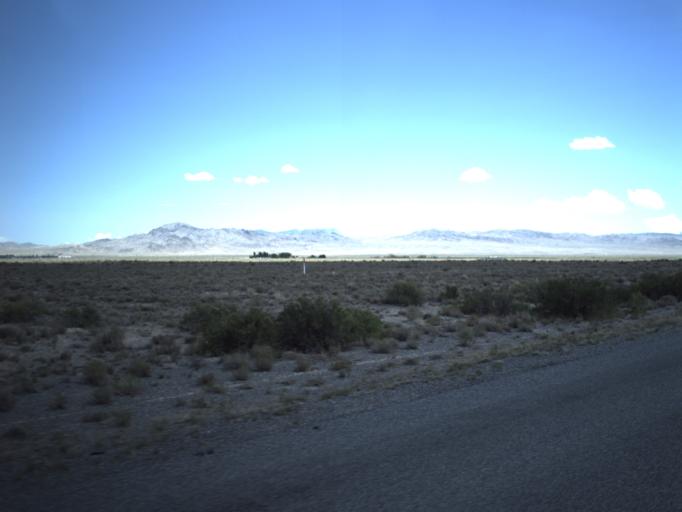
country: US
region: Nevada
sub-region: White Pine County
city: McGill
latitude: 39.0538
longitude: -114.0055
